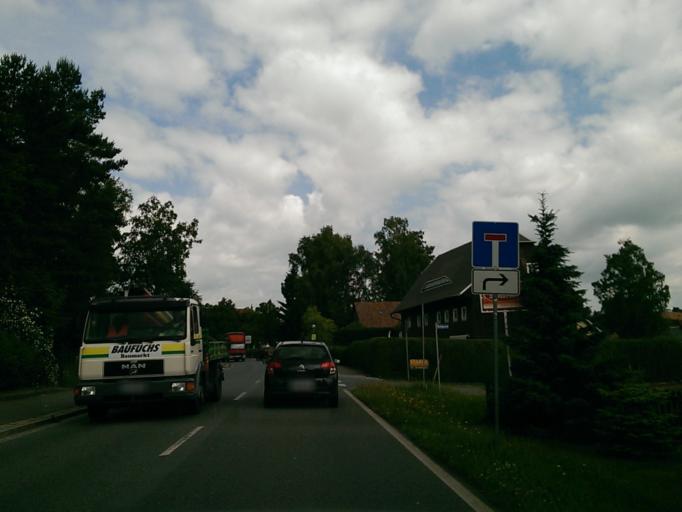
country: DE
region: Saxony
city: Mittelherwigsdorf
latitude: 50.9487
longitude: 14.7356
